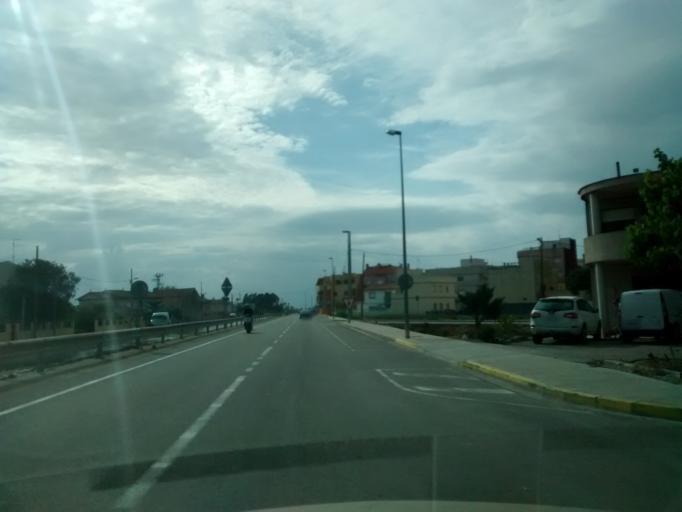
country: ES
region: Catalonia
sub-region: Provincia de Tarragona
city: Deltebre
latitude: 40.7043
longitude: 0.7161
